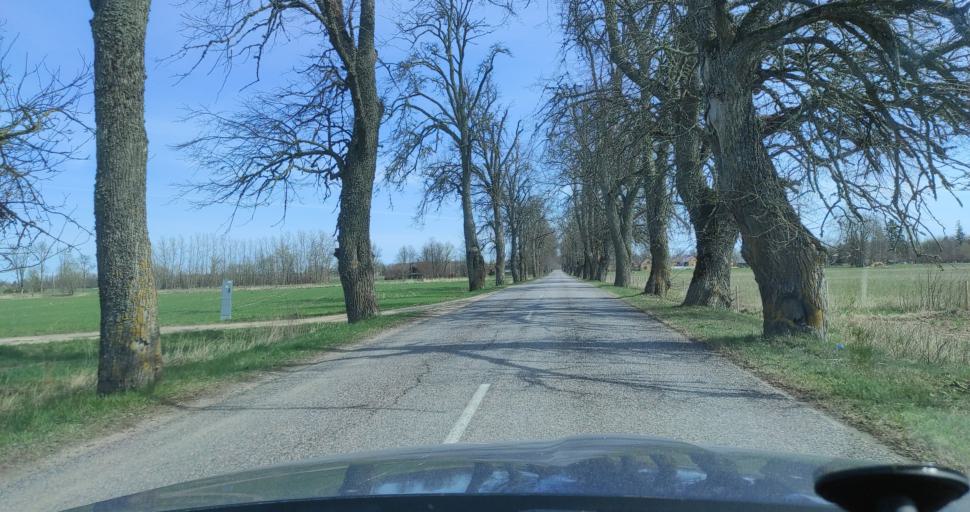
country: LV
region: Talsu Rajons
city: Stende
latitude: 57.2194
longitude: 22.5063
